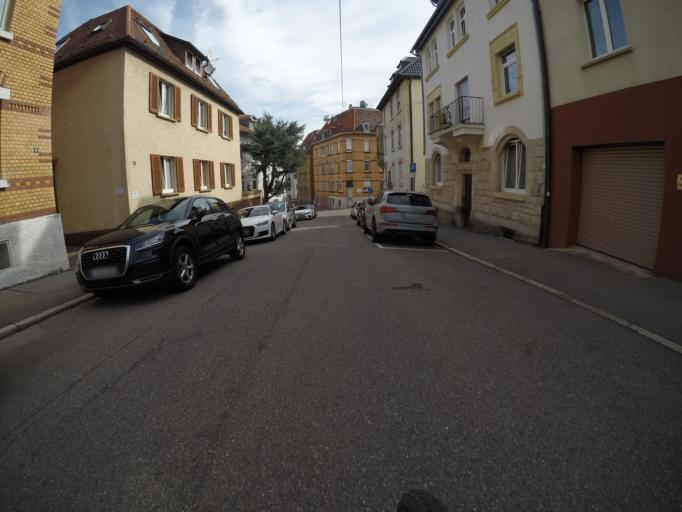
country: DE
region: Baden-Wuerttemberg
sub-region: Regierungsbezirk Stuttgart
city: Stuttgart
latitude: 48.7594
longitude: 9.1573
